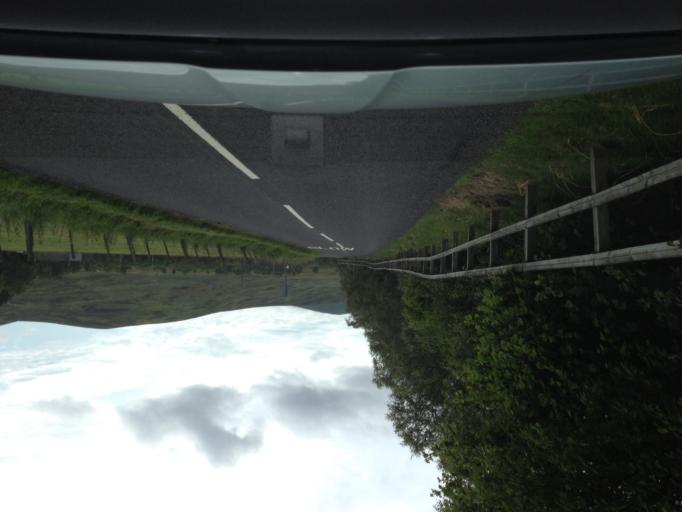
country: GB
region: Scotland
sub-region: Aberdeenshire
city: Aboyne
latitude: 56.9061
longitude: -2.8367
